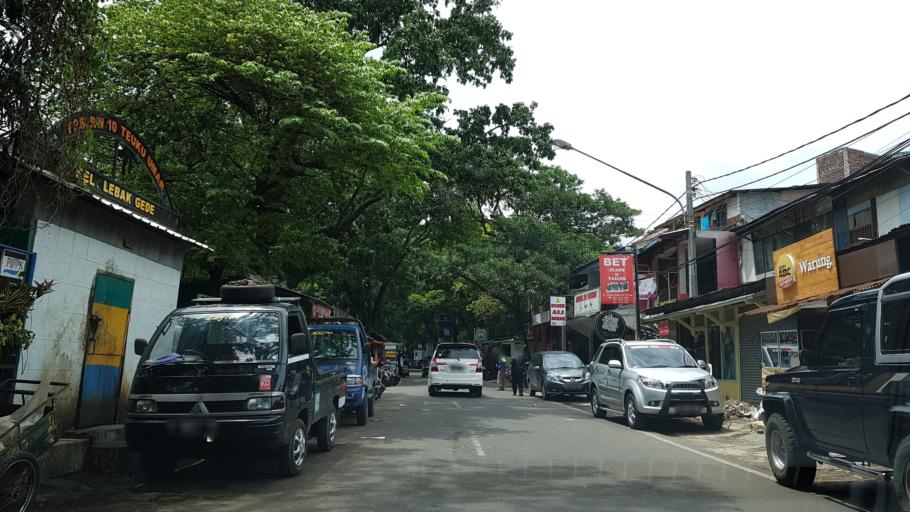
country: ID
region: West Java
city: Bandung
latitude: -6.8921
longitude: 107.6171
